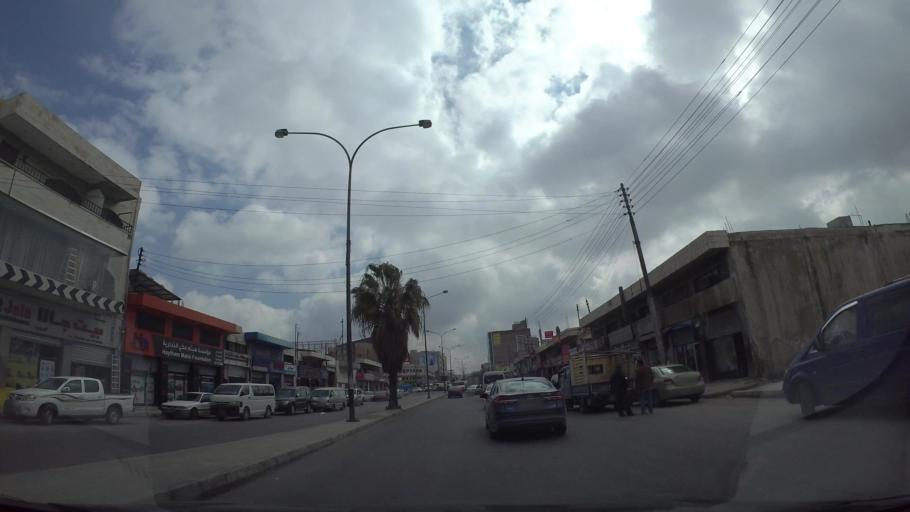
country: JO
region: Amman
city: Al Quwaysimah
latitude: 31.9225
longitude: 35.9381
